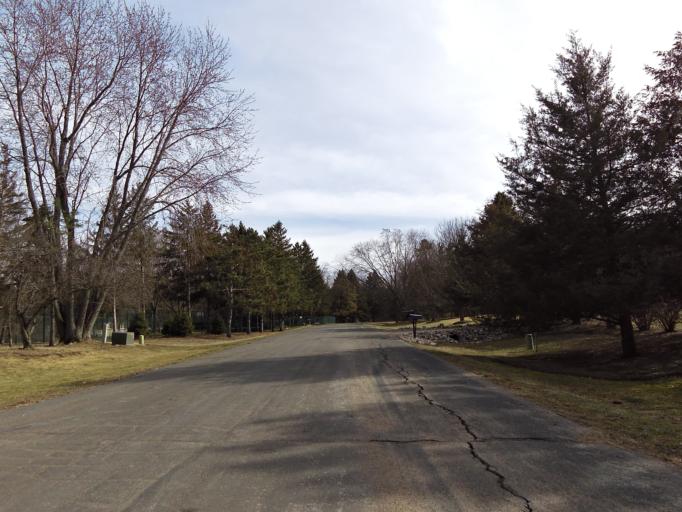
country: US
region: Minnesota
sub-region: Washington County
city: Lakeland
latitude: 44.9448
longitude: -92.7837
